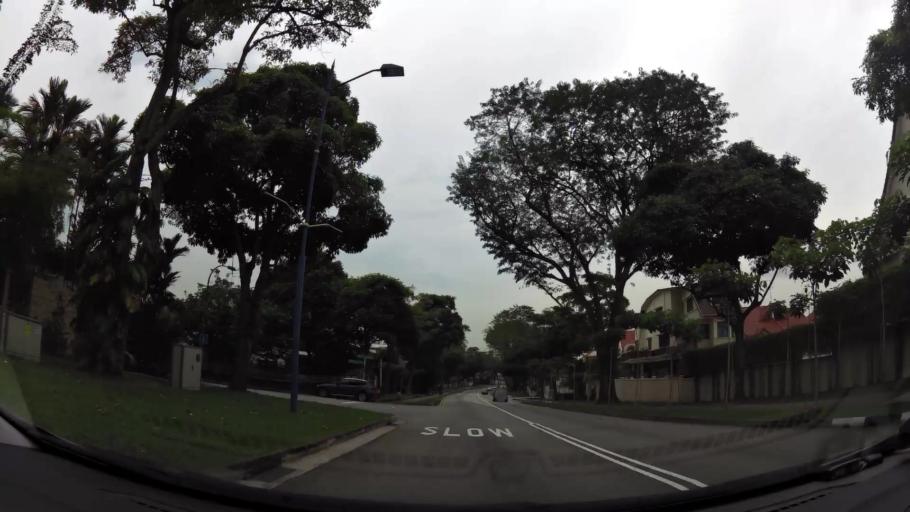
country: SG
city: Singapore
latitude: 1.3608
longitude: 103.8681
